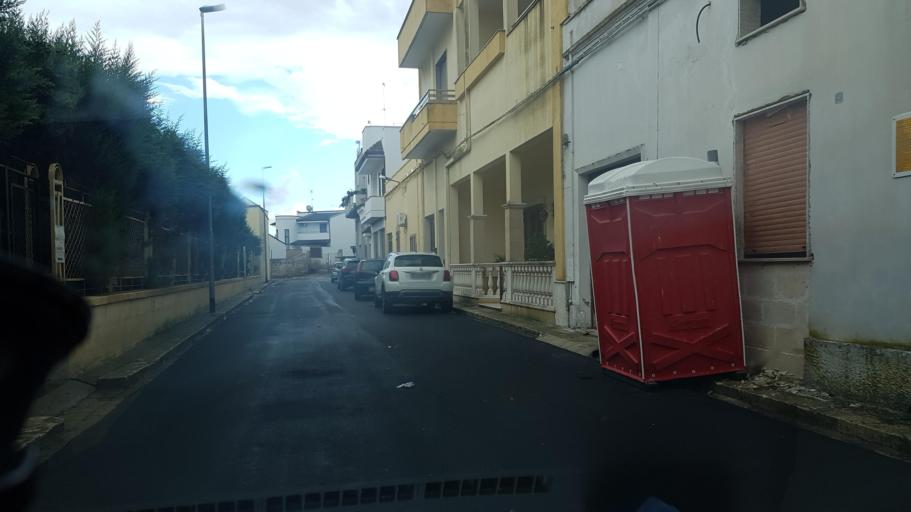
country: IT
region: Apulia
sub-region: Provincia di Lecce
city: Carmiano
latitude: 40.3468
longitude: 18.0511
